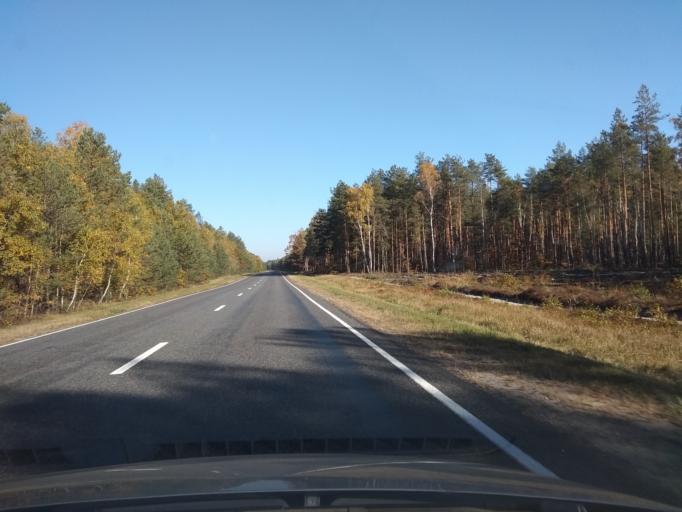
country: BY
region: Brest
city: Malaryta
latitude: 51.9573
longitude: 24.1886
